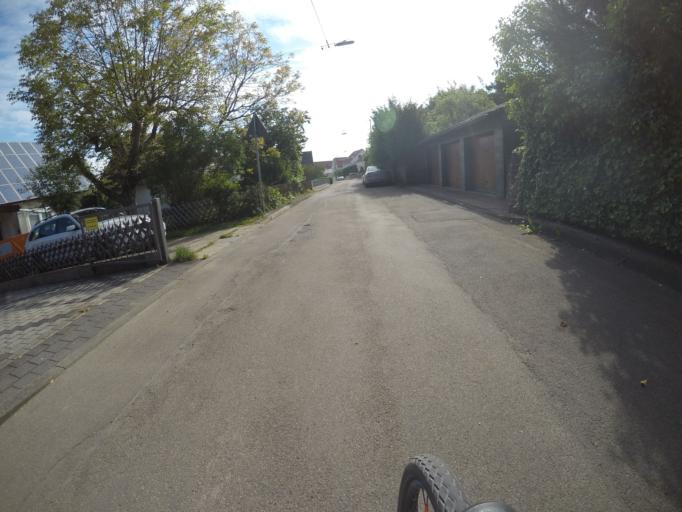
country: DE
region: Baden-Wuerttemberg
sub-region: Regierungsbezirk Stuttgart
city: Neuhausen auf den Fildern
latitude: 48.6763
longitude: 9.2801
